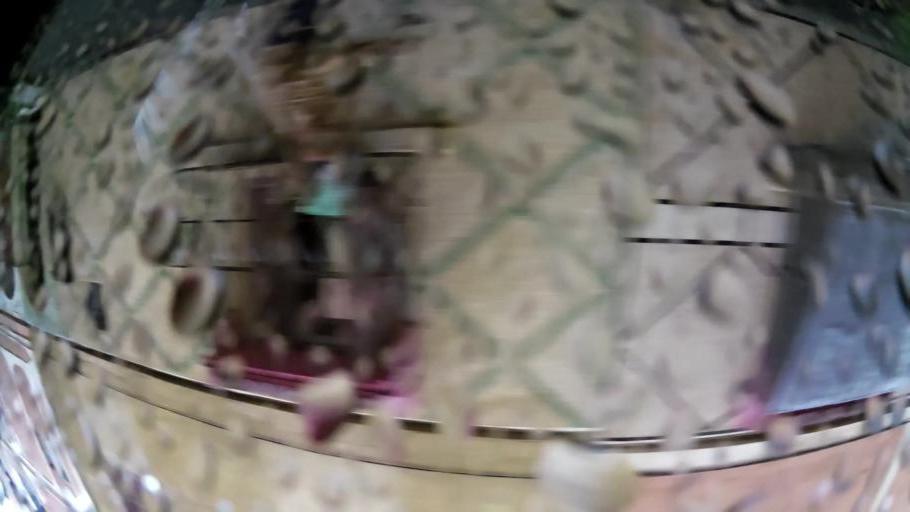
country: MA
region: Grand Casablanca
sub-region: Mediouna
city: Tit Mellil
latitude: 33.5702
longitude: -7.5311
